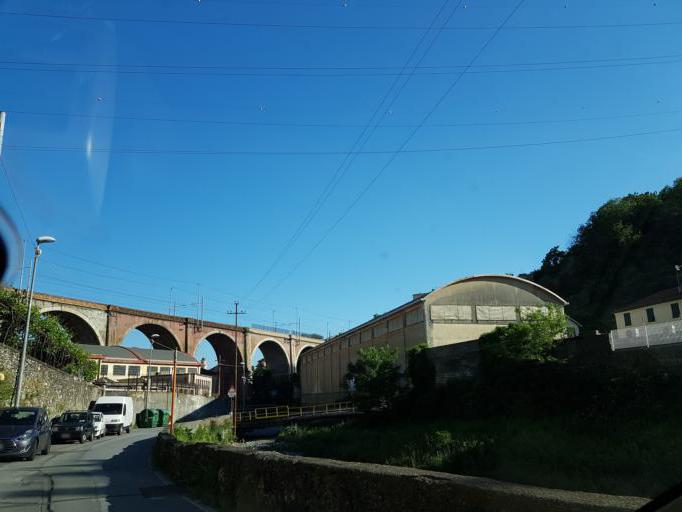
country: IT
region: Liguria
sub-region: Provincia di Genova
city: Genoa
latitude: 44.4549
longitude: 8.8895
